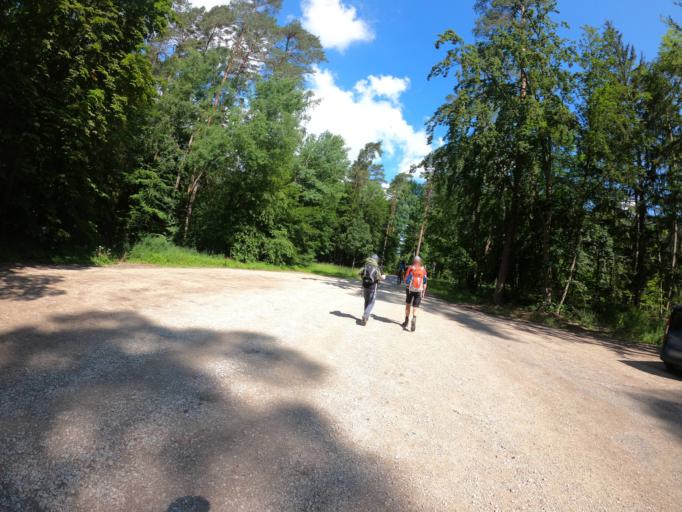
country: DE
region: Bavaria
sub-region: Upper Franconia
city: Memmelsdorf
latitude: 49.8888
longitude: 10.9544
